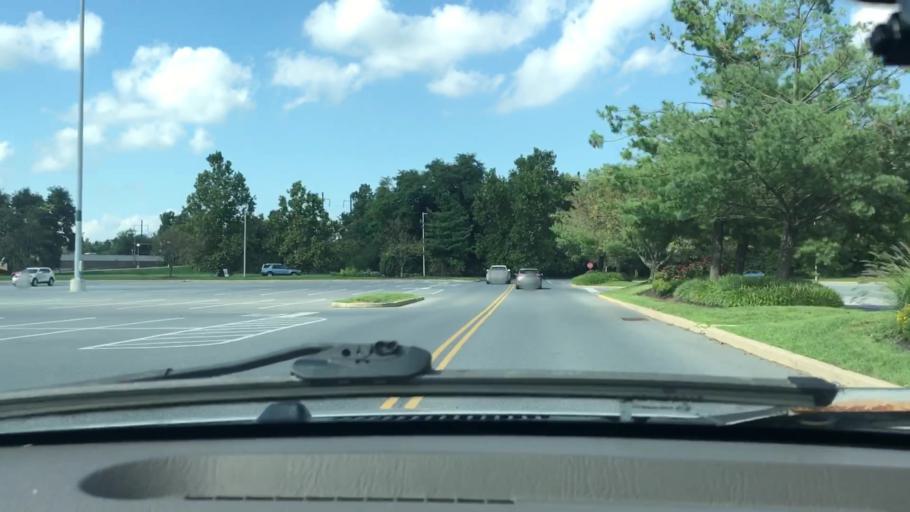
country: US
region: Pennsylvania
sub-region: Lancaster County
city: East Petersburg
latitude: 40.0683
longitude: -76.3373
